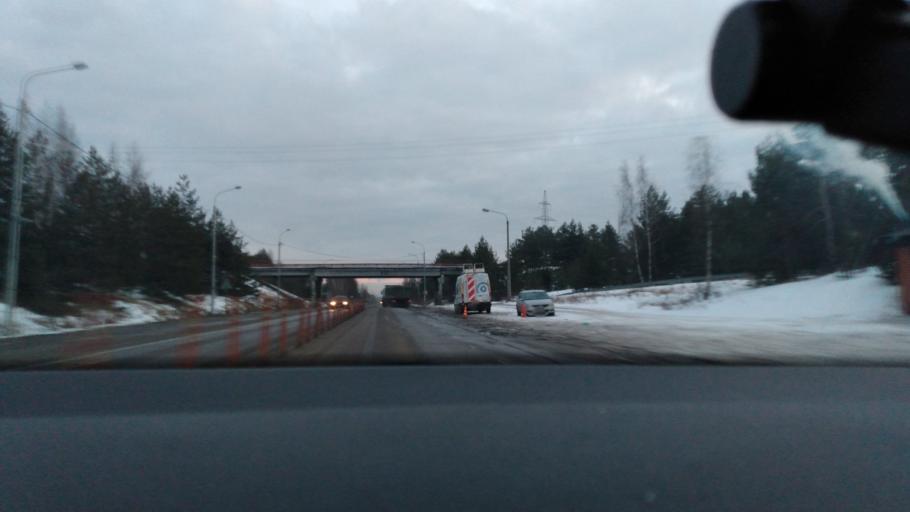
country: RU
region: Moskovskaya
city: Yegor'yevsk
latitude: 55.4165
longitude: 39.0445
